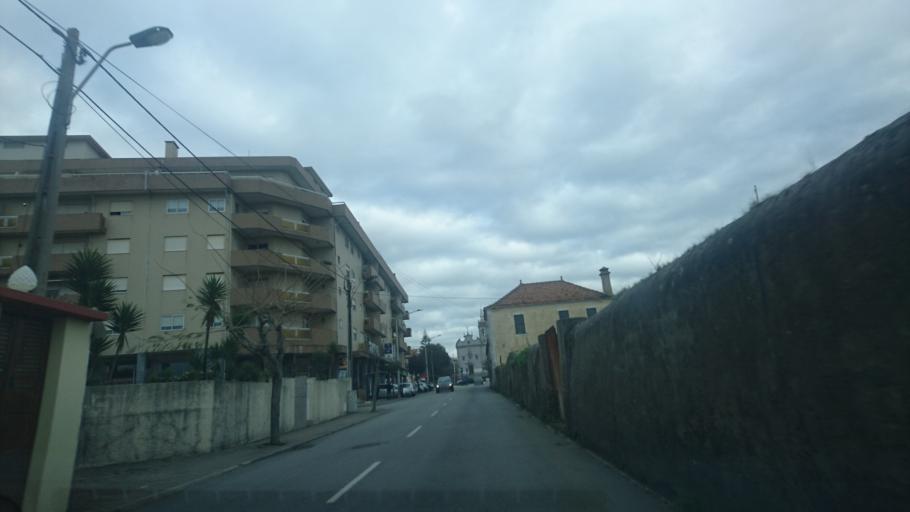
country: PT
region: Aveiro
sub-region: Ovar
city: Esmoriz
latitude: 40.9556
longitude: -8.6277
